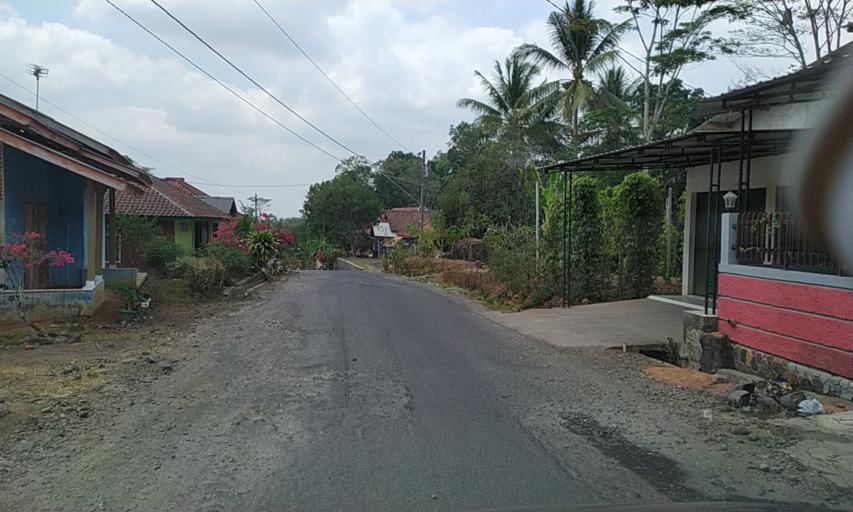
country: ID
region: Central Java
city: Karanganyar
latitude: -7.3329
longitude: 108.6295
